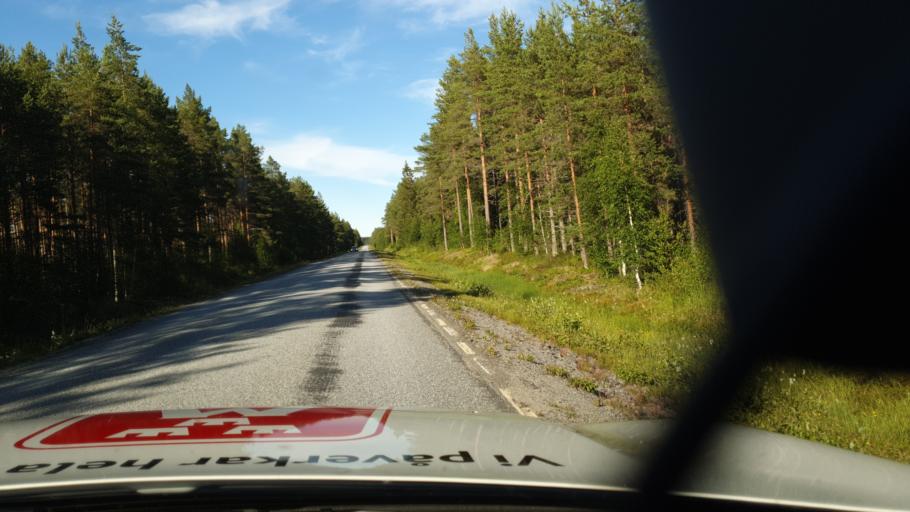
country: SE
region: Vaesterbotten
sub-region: Umea Kommun
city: Saevar
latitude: 63.8873
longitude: 20.7329
